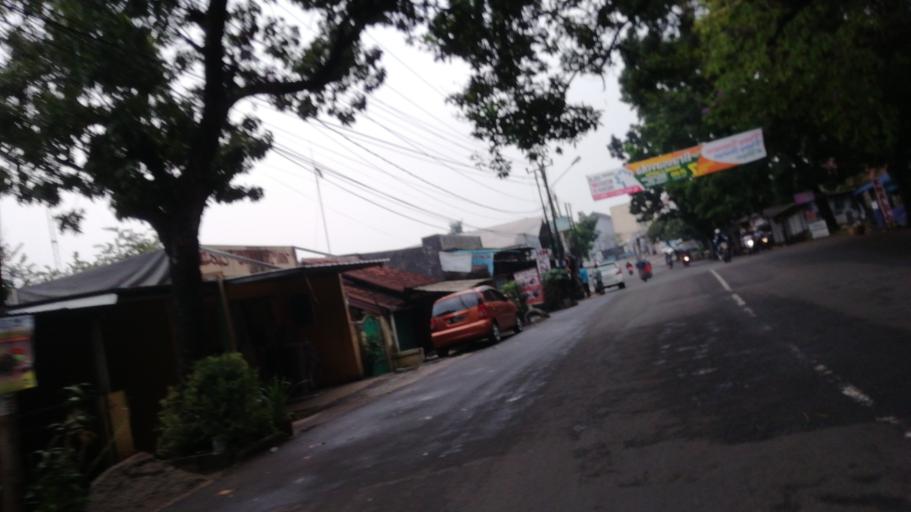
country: ID
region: West Java
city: Cibinong
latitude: -6.5257
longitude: 106.8090
